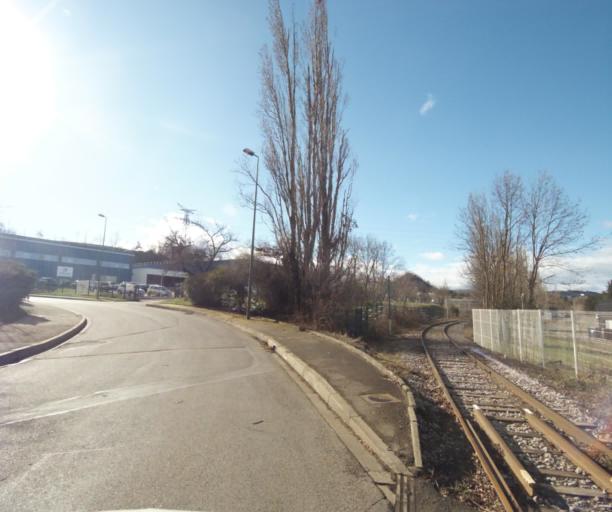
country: FR
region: Rhone-Alpes
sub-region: Departement de la Loire
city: La Talaudiere
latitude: 45.4617
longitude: 4.4253
